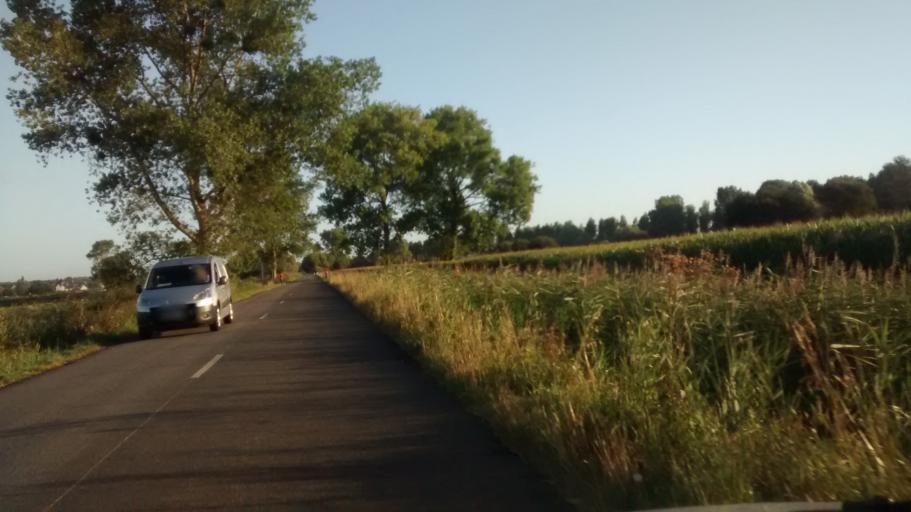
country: FR
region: Brittany
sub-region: Departement d'Ille-et-Vilaine
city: La Gouesniere
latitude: 48.5648
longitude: -1.8759
